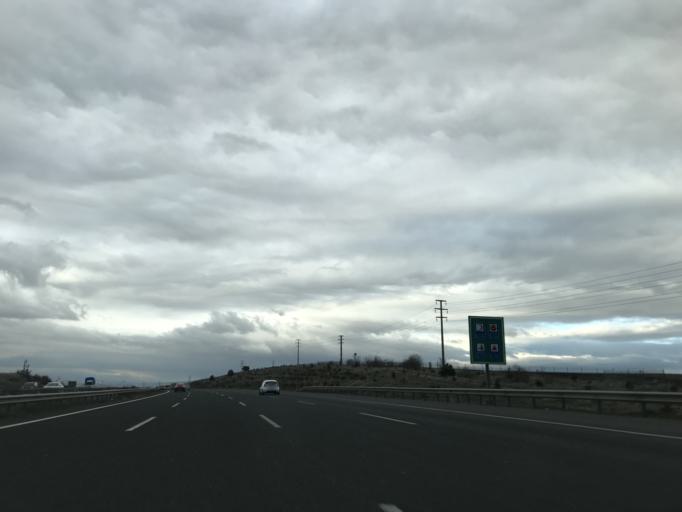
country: TR
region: Ankara
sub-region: Goelbasi
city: Golbasi
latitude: 39.7764
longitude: 32.6868
